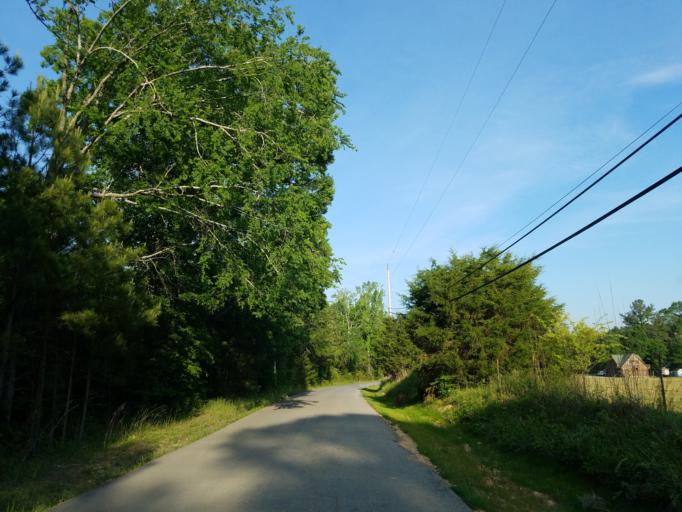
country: US
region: Georgia
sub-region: Floyd County
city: Shannon
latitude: 34.4931
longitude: -85.1221
